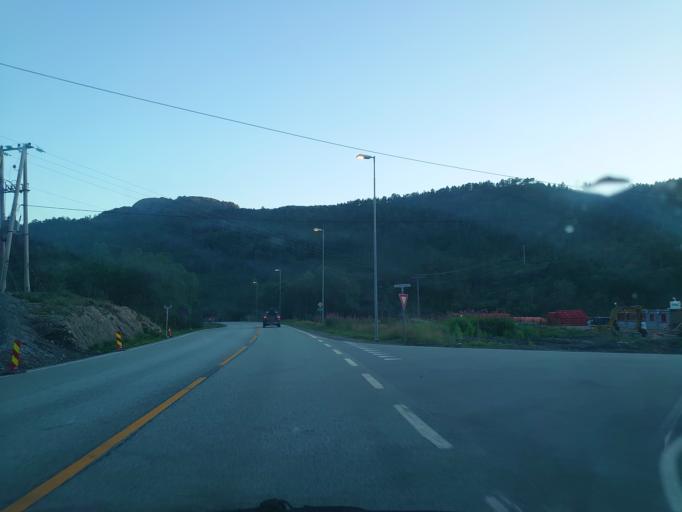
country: NO
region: Hordaland
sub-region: Osteroy
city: Lonevag
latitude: 60.6648
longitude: 5.4864
